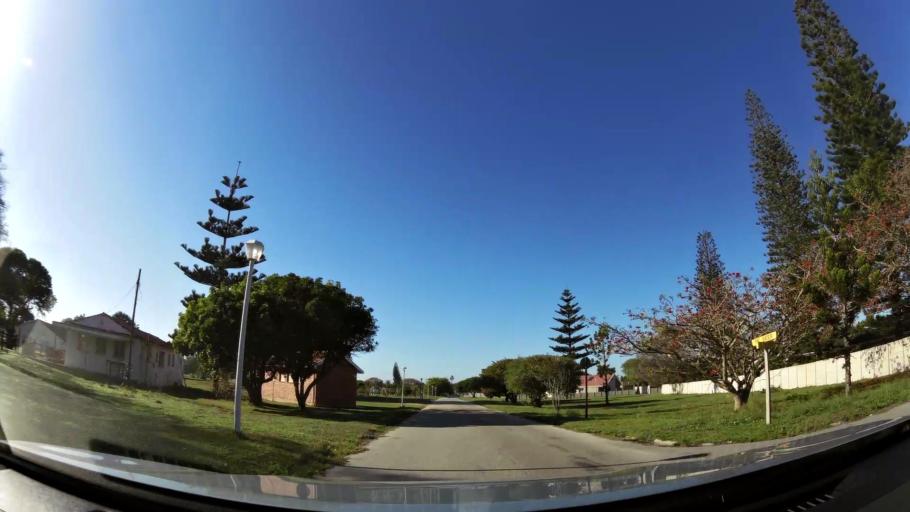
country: ZA
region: Eastern Cape
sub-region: Nelson Mandela Bay Metropolitan Municipality
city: Port Elizabeth
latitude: -33.9864
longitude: 25.6263
